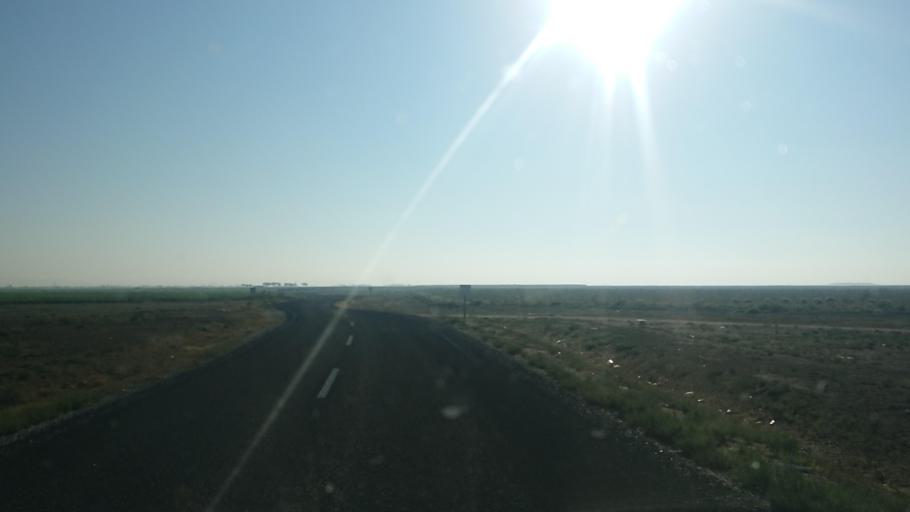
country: TR
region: Aksaray
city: Yesilova
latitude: 38.3876
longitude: 33.8047
